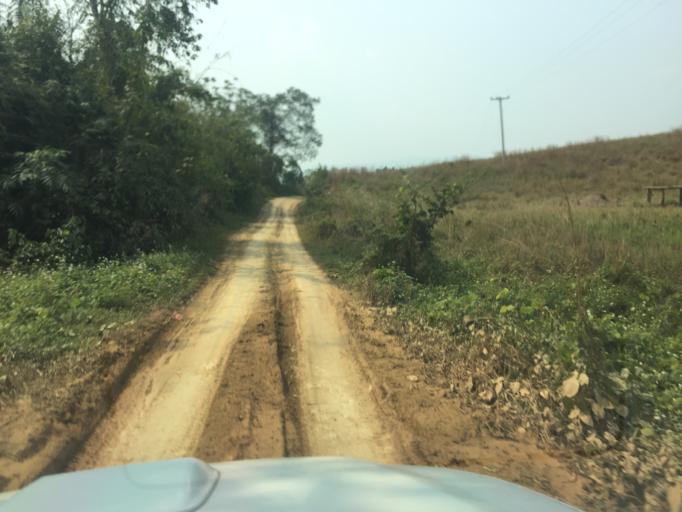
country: TH
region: Phayao
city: Phu Sang
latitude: 19.5891
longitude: 100.5259
